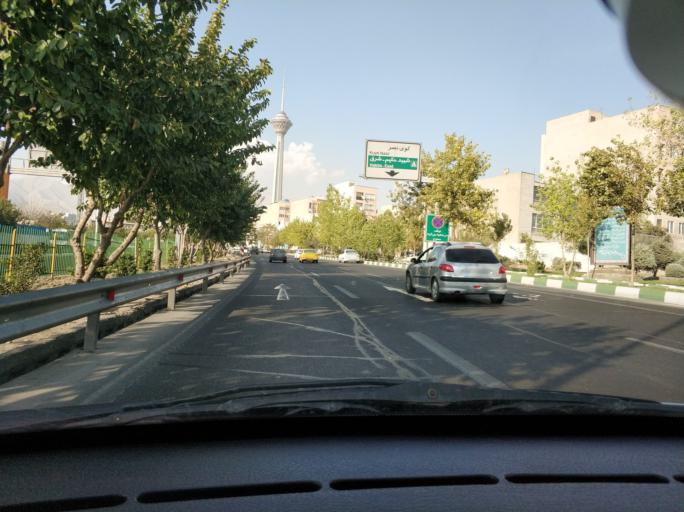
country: IR
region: Tehran
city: Tehran
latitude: 35.7317
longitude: 51.3711
